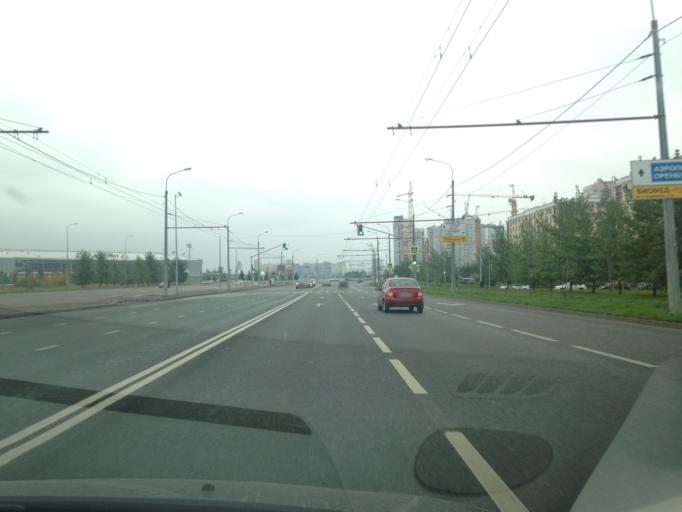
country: RU
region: Tatarstan
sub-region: Gorod Kazan'
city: Kazan
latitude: 55.7886
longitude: 49.1876
